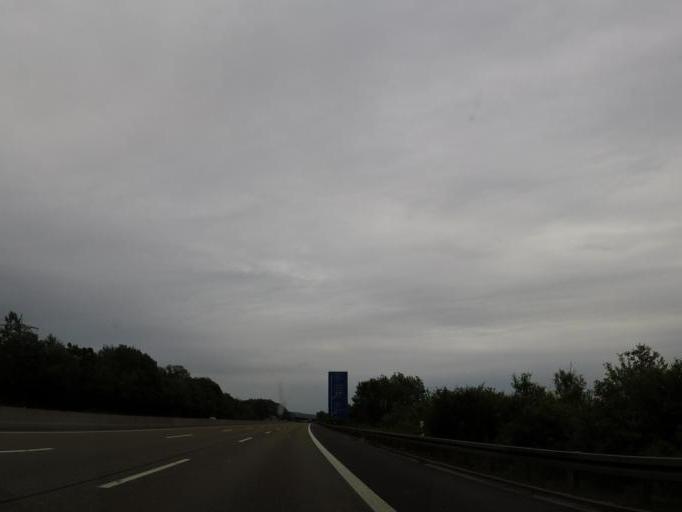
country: DE
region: Hesse
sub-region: Regierungsbezirk Kassel
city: Kirchheim
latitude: 50.8469
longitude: 9.5845
